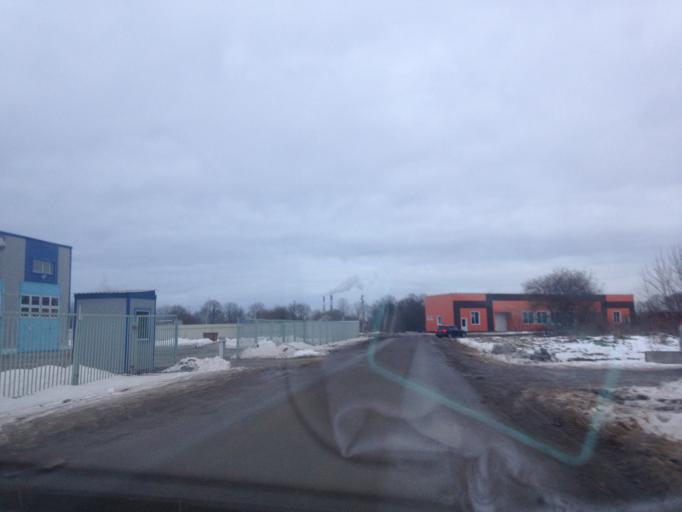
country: RU
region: Tula
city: Shchekino
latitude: 54.0230
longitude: 37.5114
